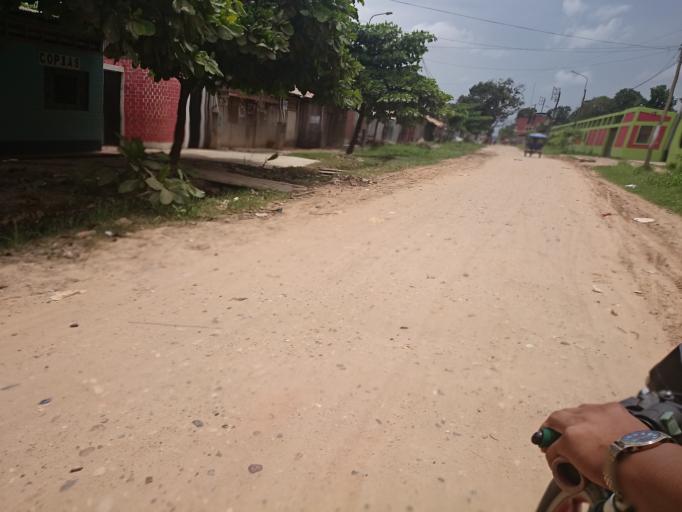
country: PE
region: Ucayali
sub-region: Provincia de Coronel Portillo
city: Pucallpa
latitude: -8.3759
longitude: -74.5578
